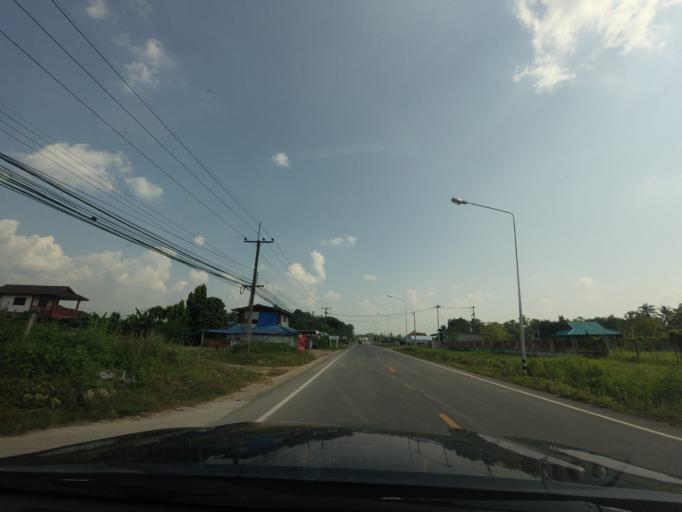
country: TH
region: Nan
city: Santi Suk
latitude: 18.9346
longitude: 100.9277
